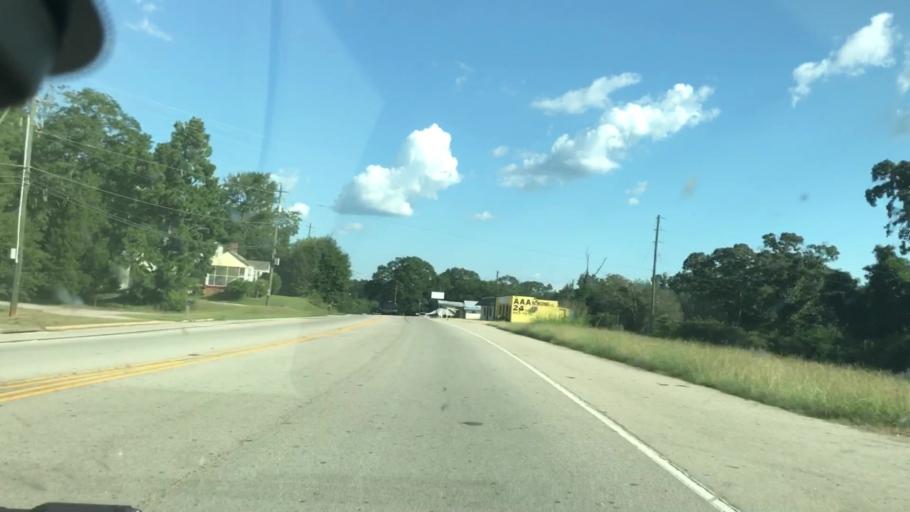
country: US
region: Georgia
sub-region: Troup County
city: La Grange
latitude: 32.9952
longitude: -85.0086
